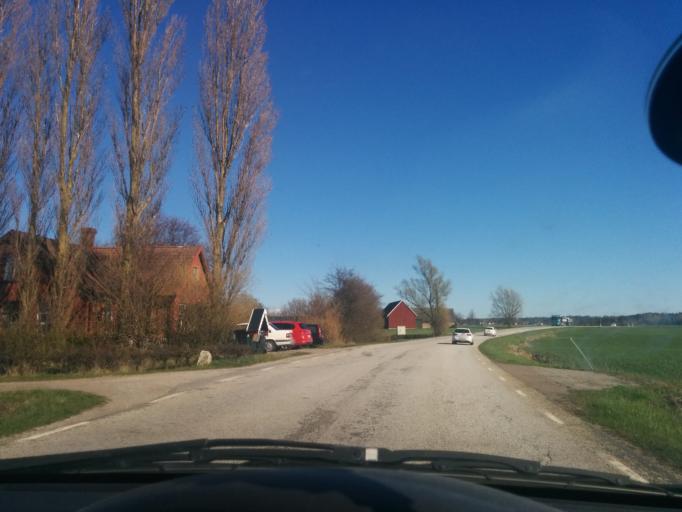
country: SE
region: Skane
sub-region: Lunds Kommun
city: Genarp
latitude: 55.6089
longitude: 13.3648
